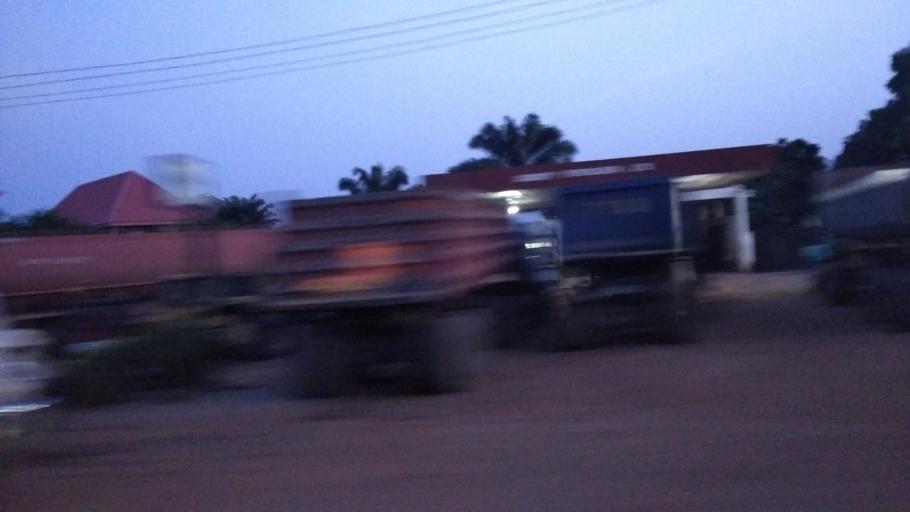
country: NG
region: Enugu
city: Enugu
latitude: 6.4654
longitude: 7.5934
